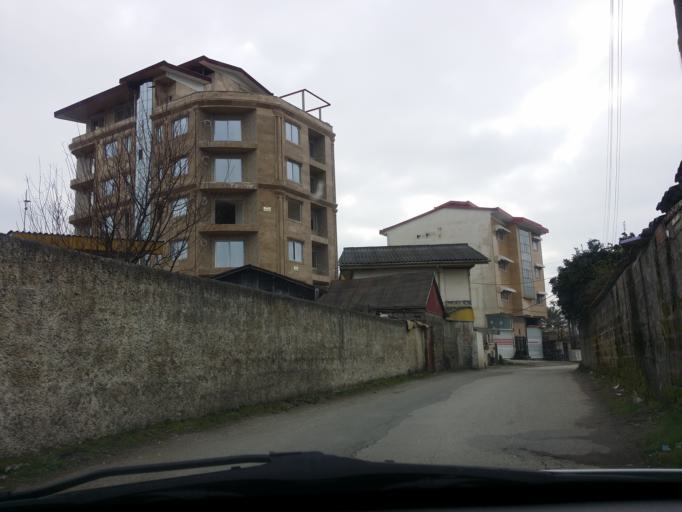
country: IR
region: Mazandaran
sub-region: Nowshahr
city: Nowshahr
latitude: 36.6558
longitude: 51.4773
